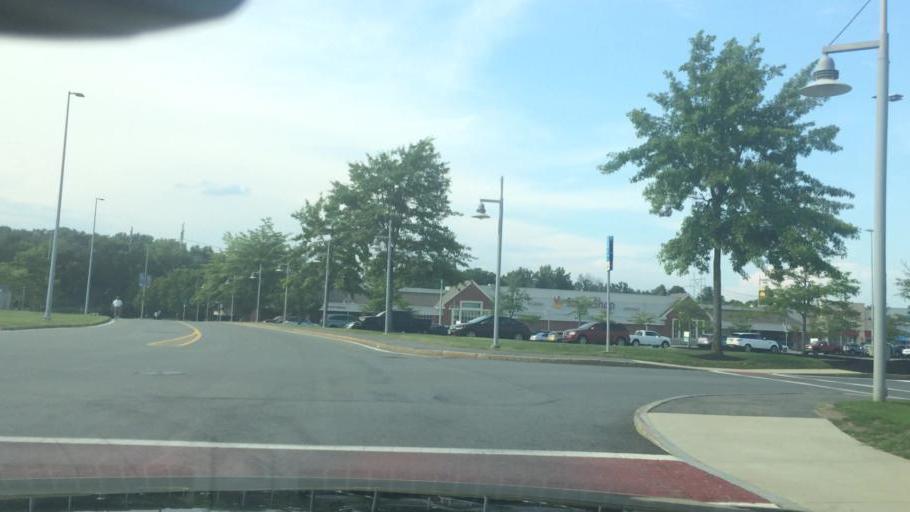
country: US
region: Massachusetts
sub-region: Essex County
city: Methuen
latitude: 42.7419
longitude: -71.1605
